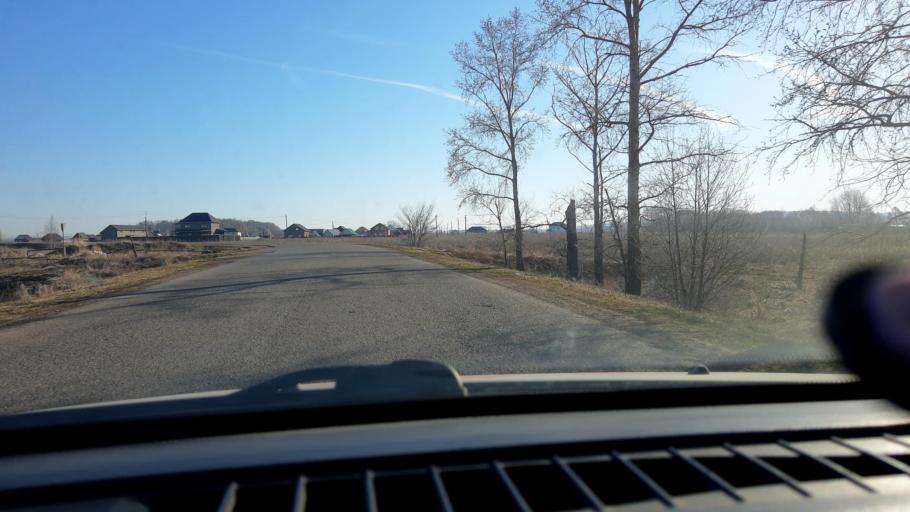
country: RU
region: Bashkortostan
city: Asanovo
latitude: 54.9730
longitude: 55.5443
